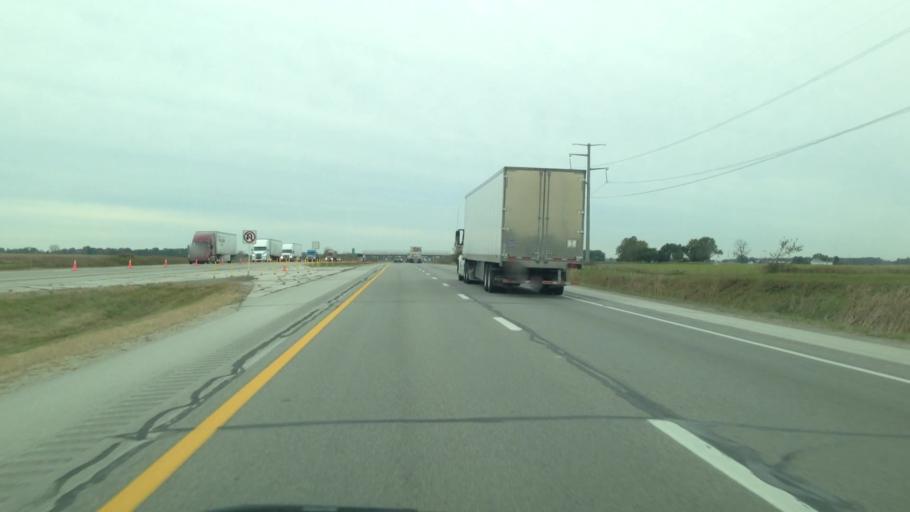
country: US
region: Ohio
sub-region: Fulton County
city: Delta
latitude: 41.5981
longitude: -83.9809
